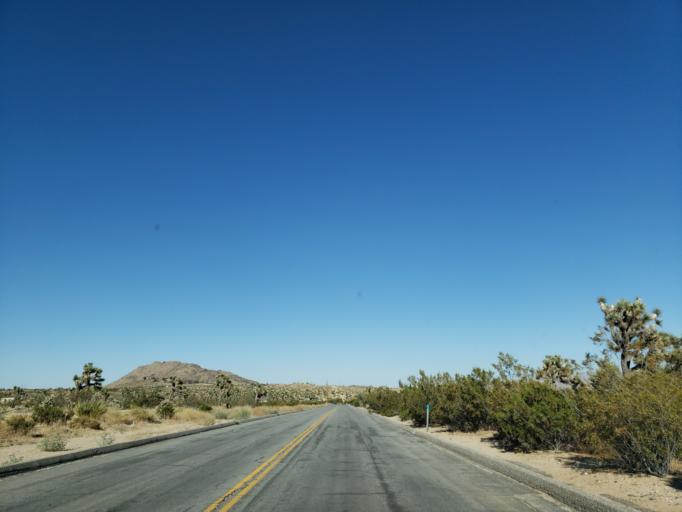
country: US
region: California
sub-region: San Bernardino County
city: Joshua Tree
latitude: 34.1640
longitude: -116.3736
